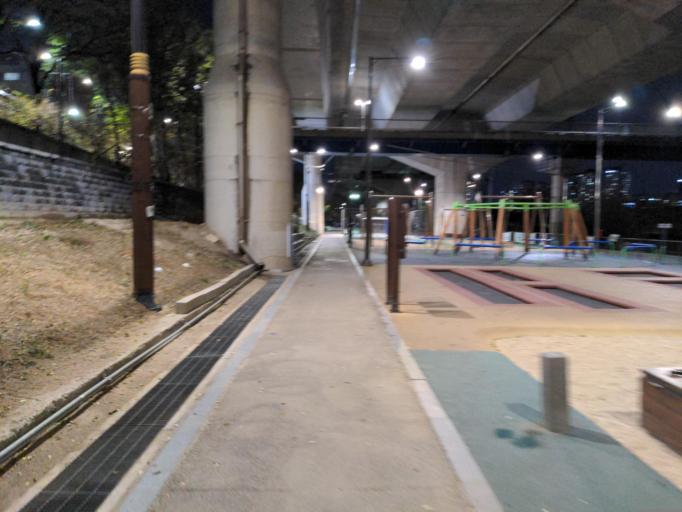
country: KR
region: Seoul
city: Seoul
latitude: 37.5615
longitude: 127.0493
